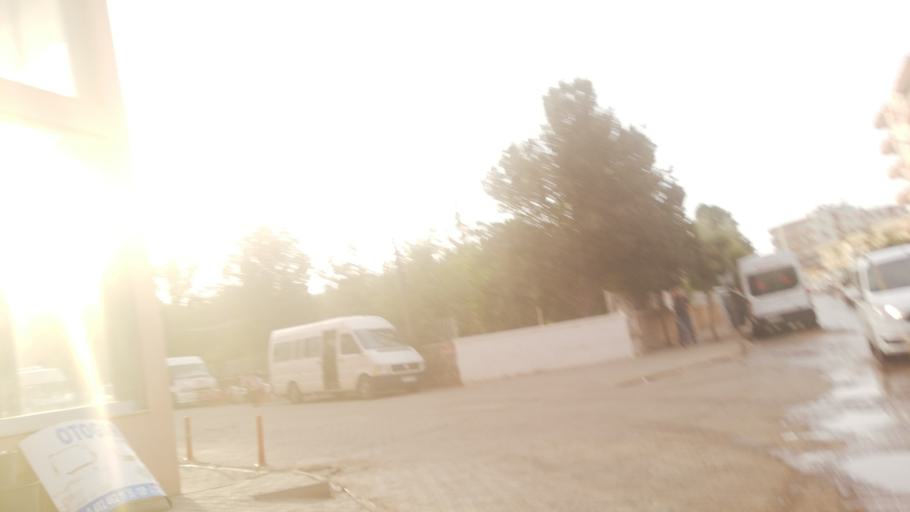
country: TR
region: Mardin
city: Midyat
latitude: 37.4277
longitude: 41.3394
